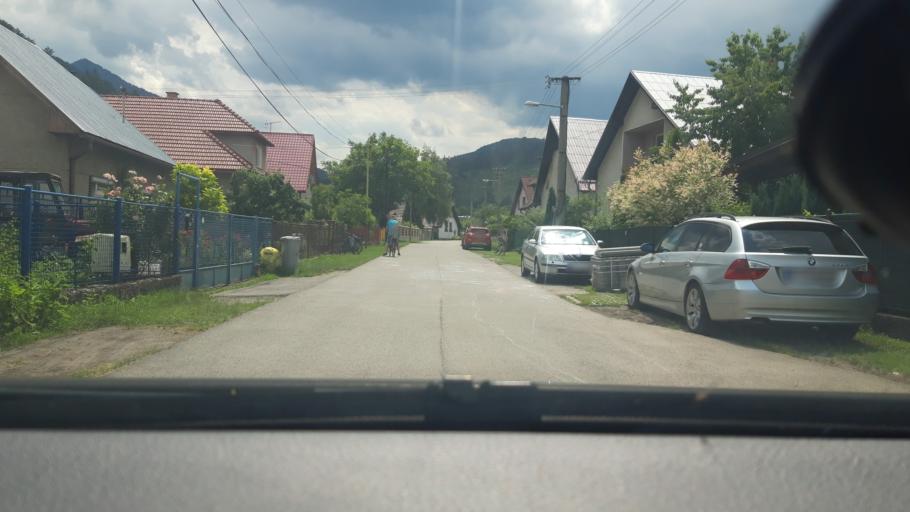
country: SK
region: Zilinsky
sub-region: Okres Martin
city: Martin
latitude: 48.9359
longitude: 18.9246
